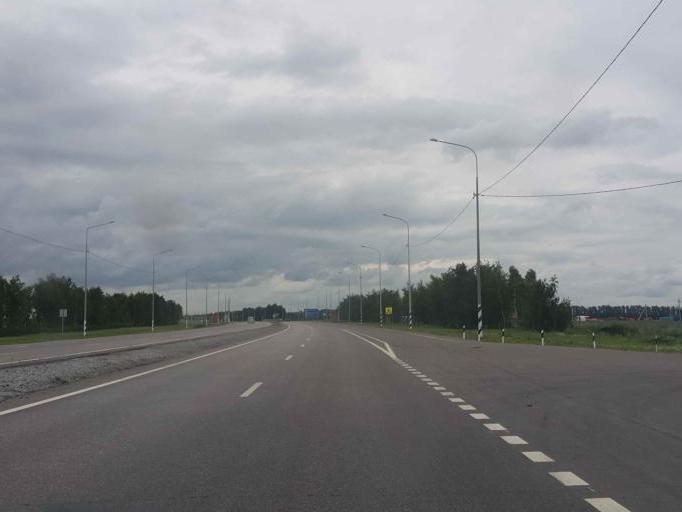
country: RU
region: Tambov
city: Zavoronezhskoye
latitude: 52.8613
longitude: 40.7669
